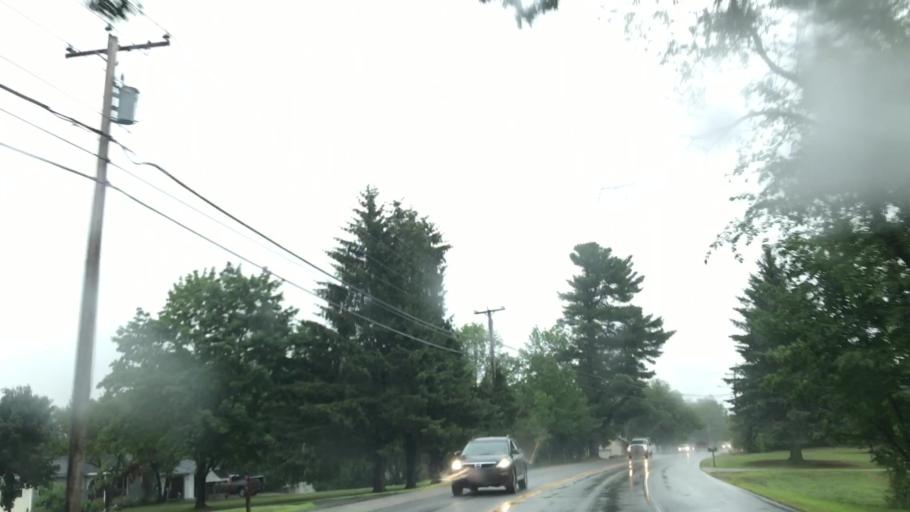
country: US
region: Maine
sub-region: York County
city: North Berwick
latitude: 43.3079
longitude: -70.6810
